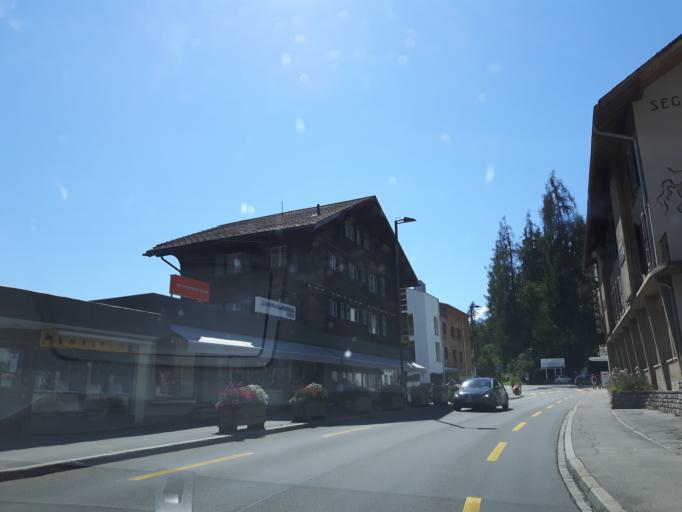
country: CH
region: Grisons
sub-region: Imboden District
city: Flims
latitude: 46.8287
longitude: 9.2878
